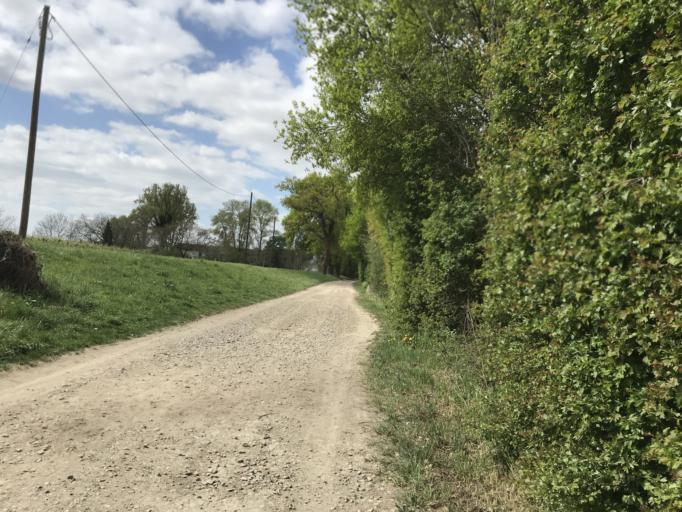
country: DE
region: Hesse
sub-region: Regierungsbezirk Darmstadt
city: Eltville
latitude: 50.0146
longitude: 8.1235
